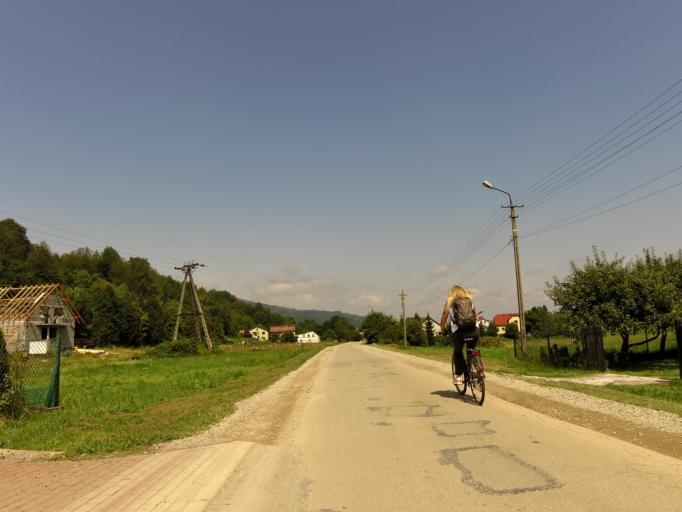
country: PL
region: Silesian Voivodeship
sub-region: Powiat zywiecki
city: Cisiec
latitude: 49.5820
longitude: 19.0920
